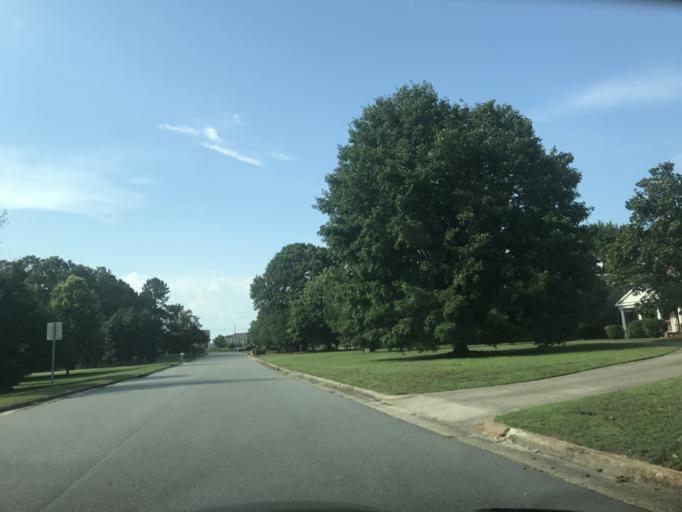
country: US
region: North Carolina
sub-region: Wake County
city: Knightdale
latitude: 35.8323
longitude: -78.5529
